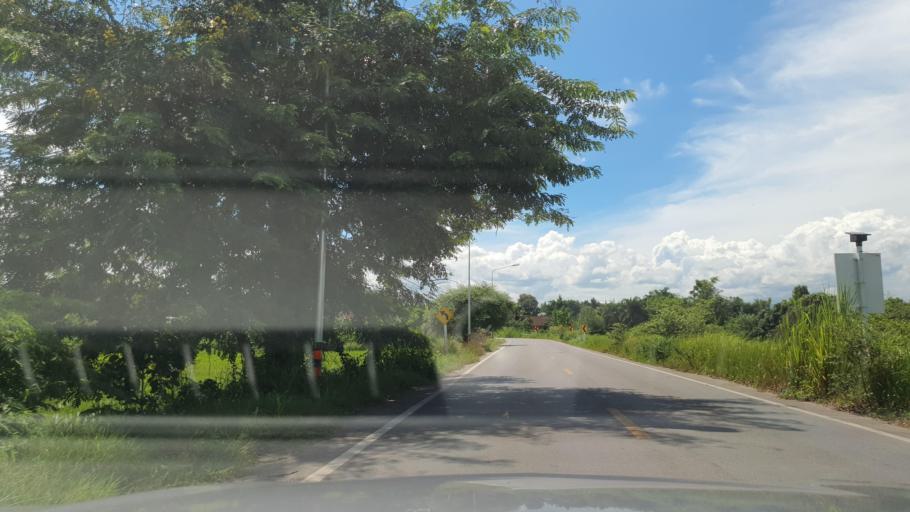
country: TH
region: Chiang Mai
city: San Pa Tong
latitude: 18.5990
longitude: 98.8993
